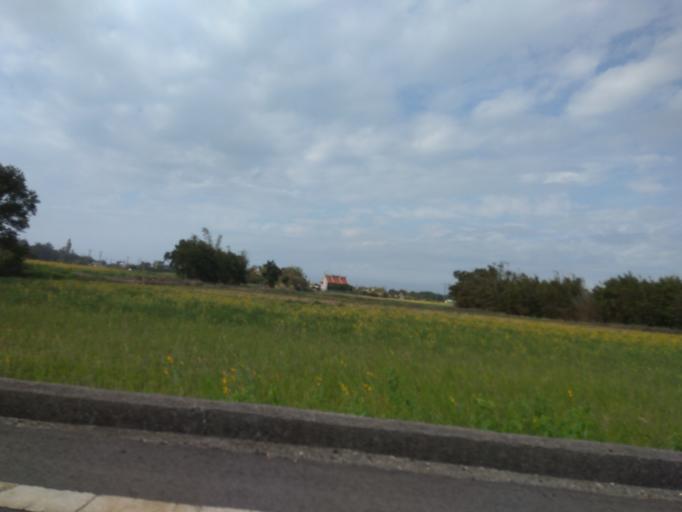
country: TW
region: Taiwan
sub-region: Hsinchu
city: Zhubei
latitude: 24.9795
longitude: 121.0324
